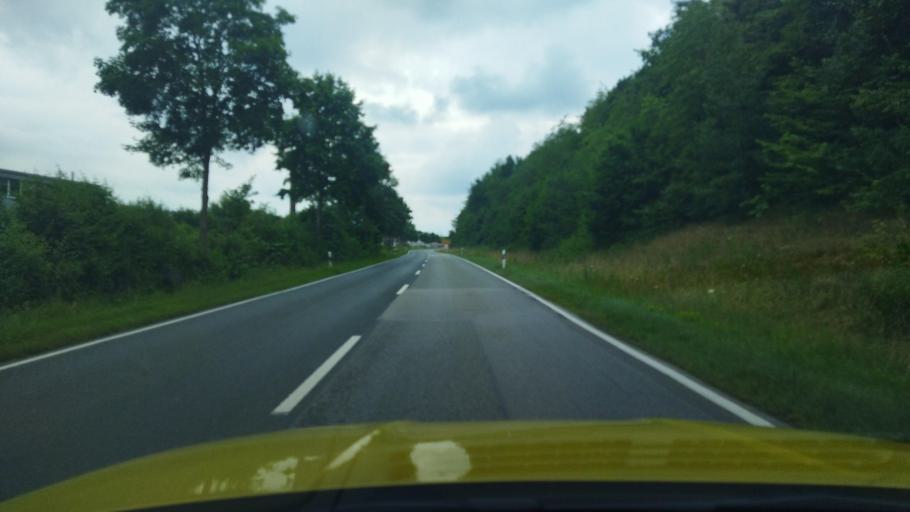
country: DE
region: Bavaria
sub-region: Regierungsbezirk Mittelfranken
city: Gunzenhausen
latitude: 49.1256
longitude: 10.7747
